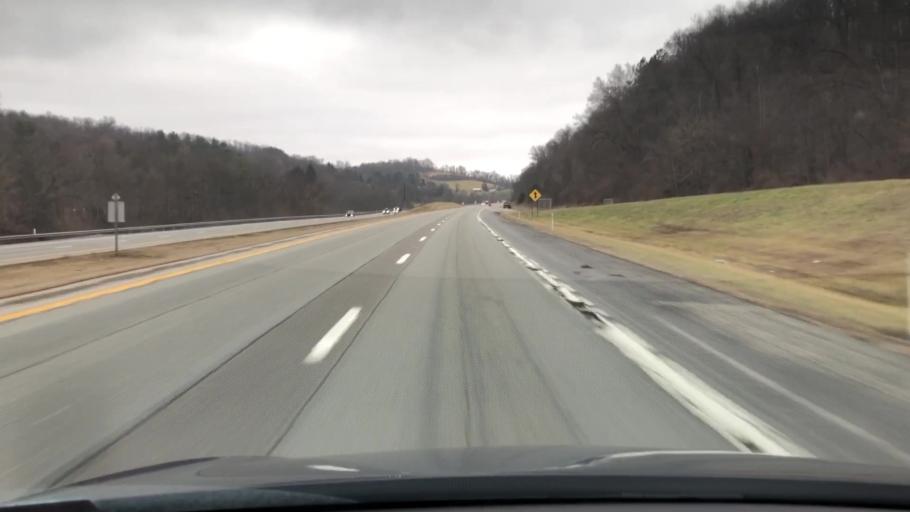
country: US
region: Pennsylvania
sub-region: Washington County
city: East Washington
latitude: 40.1219
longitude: -80.2061
